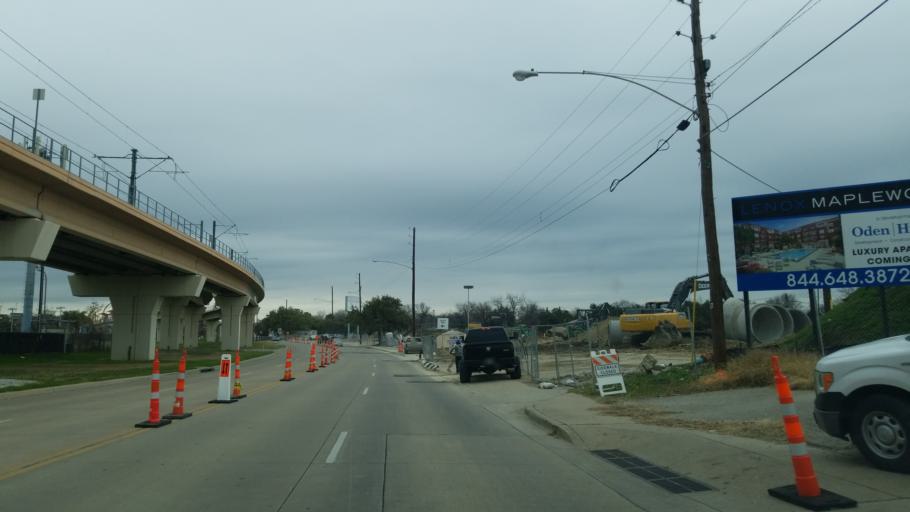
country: US
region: Texas
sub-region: Dallas County
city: Highland Park
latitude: 32.8195
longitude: -96.8327
